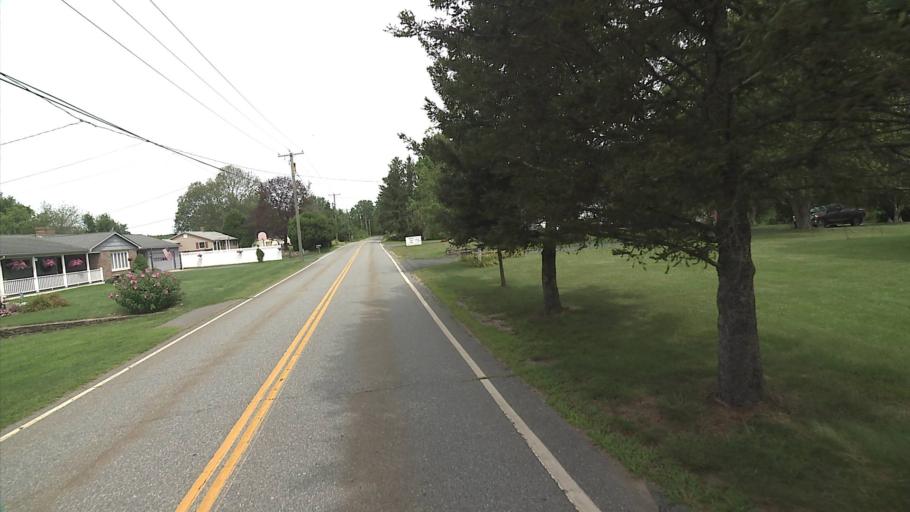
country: US
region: Connecticut
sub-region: Windham County
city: Thompson
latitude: 41.9980
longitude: -71.8451
